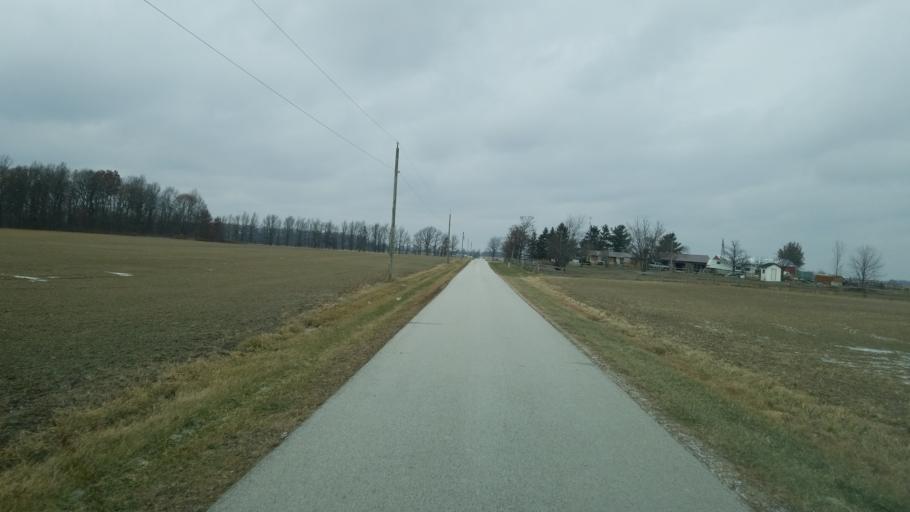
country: US
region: Ohio
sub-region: Hardin County
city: Forest
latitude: 40.7673
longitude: -83.4777
